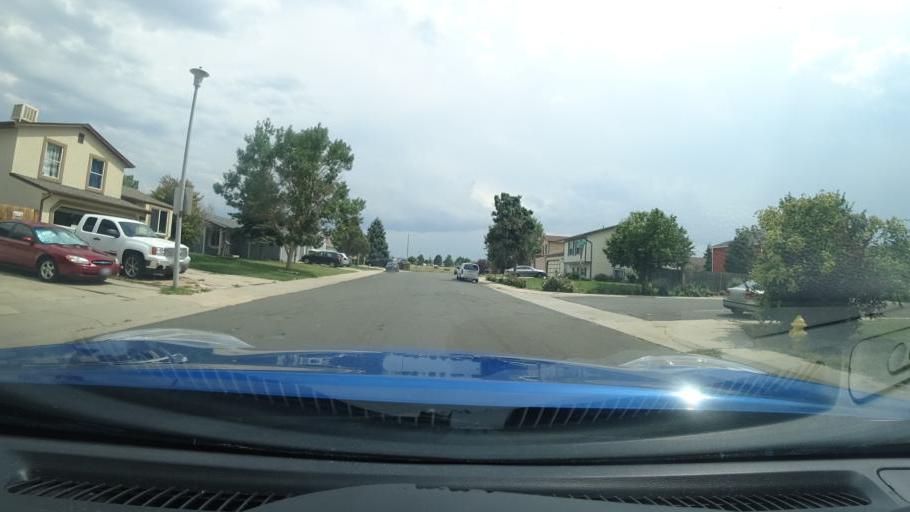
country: US
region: Colorado
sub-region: Adams County
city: Aurora
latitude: 39.6829
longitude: -104.7568
